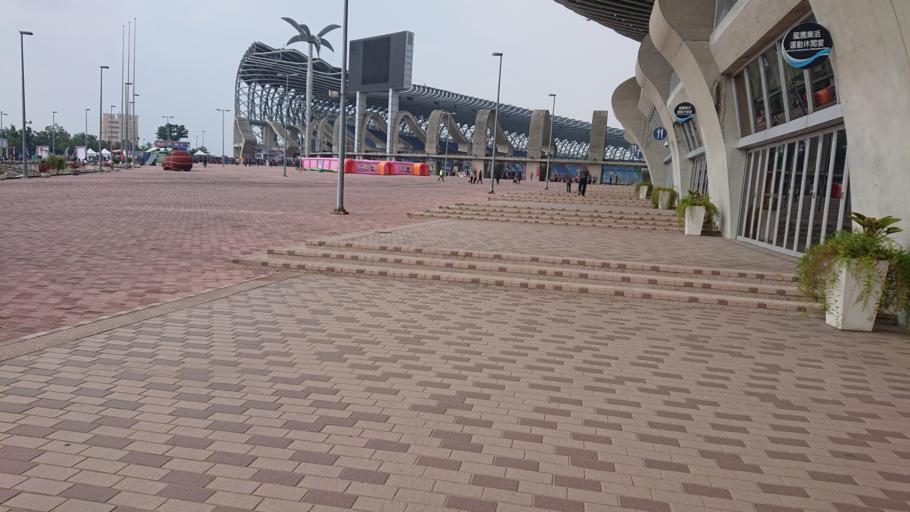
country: TW
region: Kaohsiung
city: Kaohsiung
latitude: 22.7015
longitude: 120.2960
